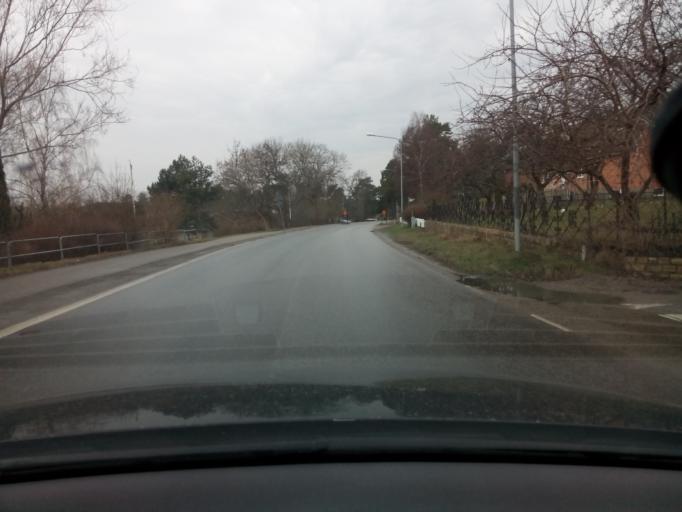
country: SE
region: Soedermanland
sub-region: Trosa Kommun
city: Trosa
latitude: 58.8986
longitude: 17.5387
